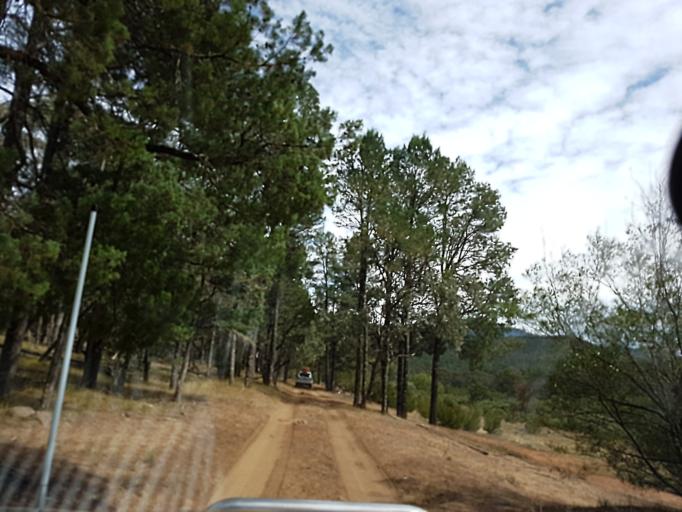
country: AU
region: New South Wales
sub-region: Snowy River
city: Jindabyne
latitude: -36.9494
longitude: 148.3989
